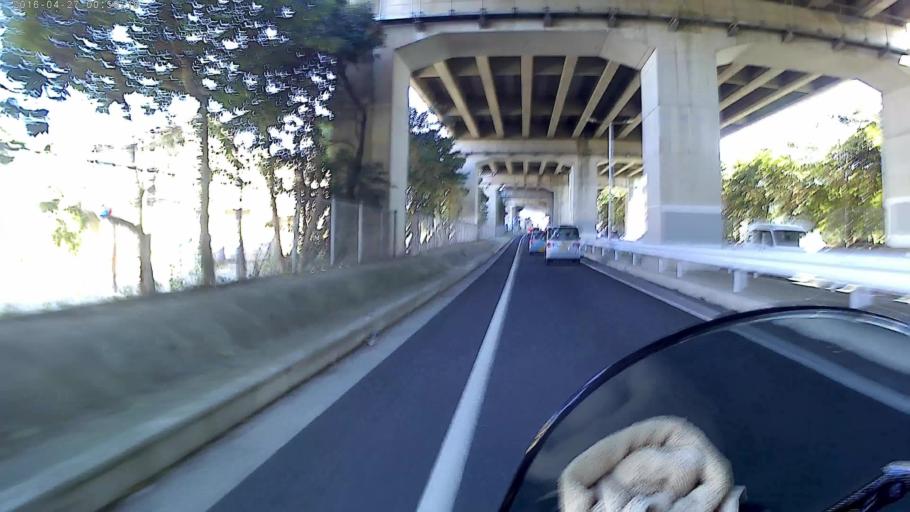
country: JP
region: Kanagawa
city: Chigasaki
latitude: 35.3502
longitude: 139.4117
